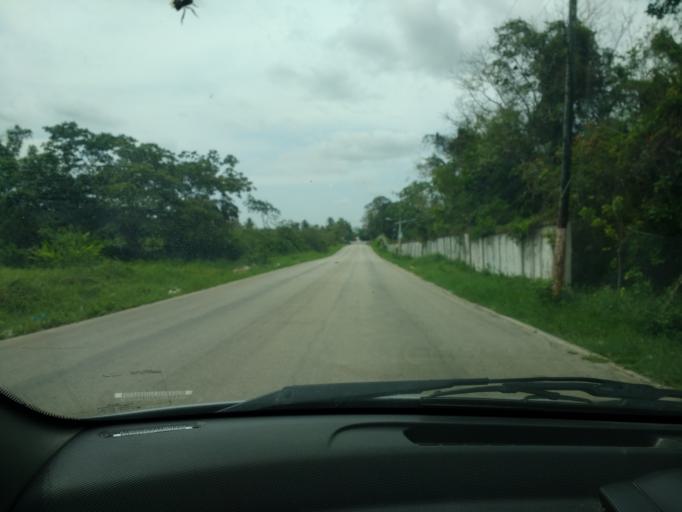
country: GT
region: Peten
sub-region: Municipio de San Benito
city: San Benito
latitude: 16.9168
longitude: -89.9291
